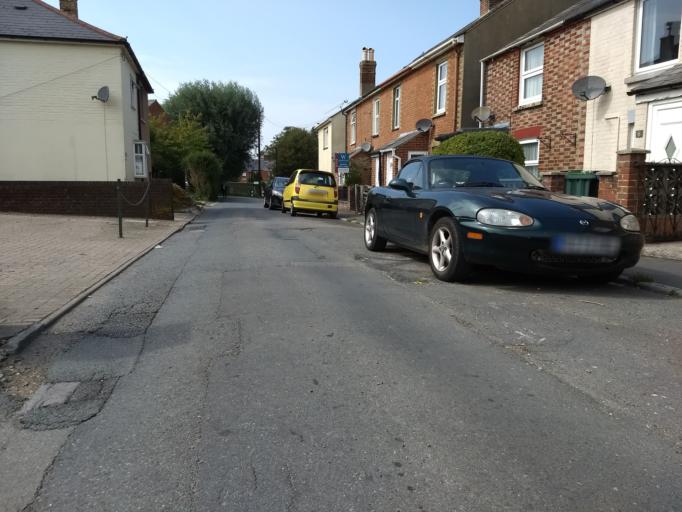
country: GB
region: England
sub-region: Isle of Wight
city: Newport
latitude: 50.7043
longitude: -1.2855
